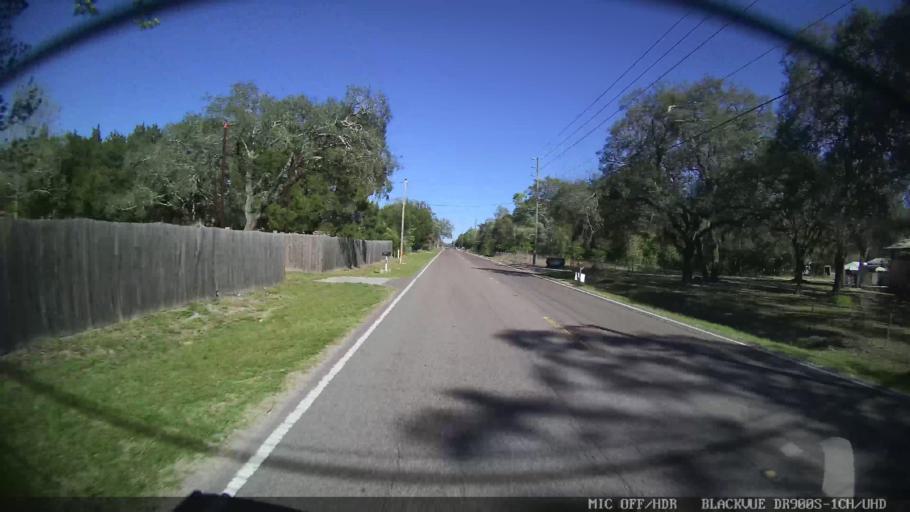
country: US
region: Florida
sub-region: Pasco County
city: Shady Hills
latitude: 28.3919
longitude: -82.5587
